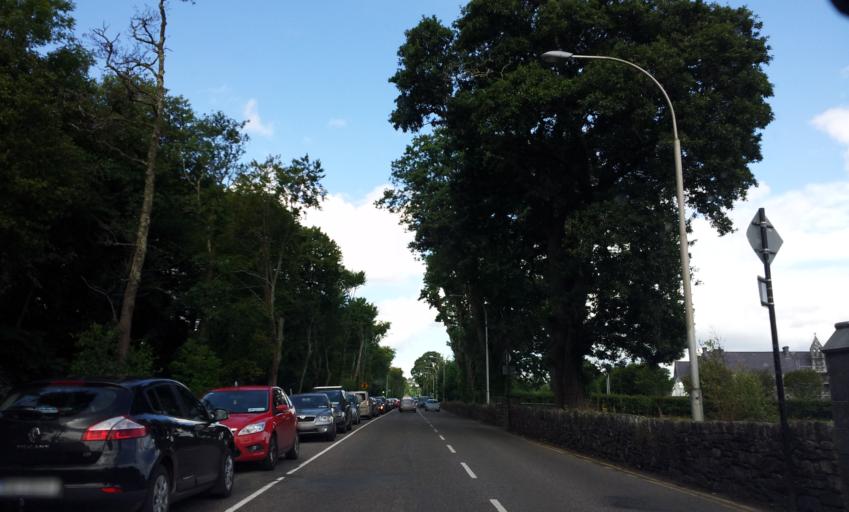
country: IE
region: Munster
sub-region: Ciarrai
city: Cill Airne
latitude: 52.0598
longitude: -9.5195
